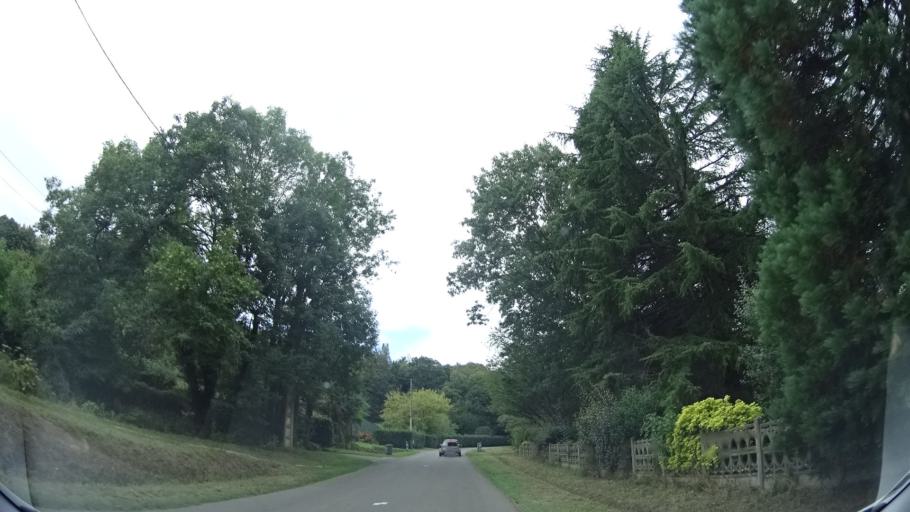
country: FR
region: Brittany
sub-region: Departement d'Ille-et-Vilaine
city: Hede-Bazouges
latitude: 48.2994
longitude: -1.7941
